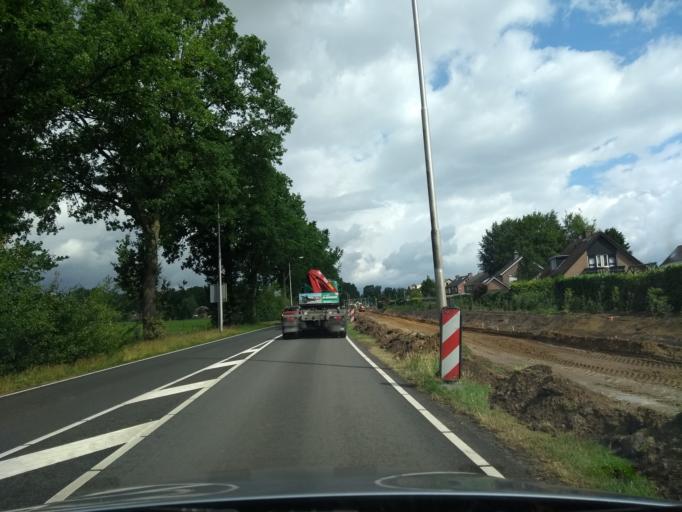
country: NL
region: Overijssel
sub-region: Gemeente Twenterand
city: Vriezenveen
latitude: 52.4001
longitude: 6.6082
